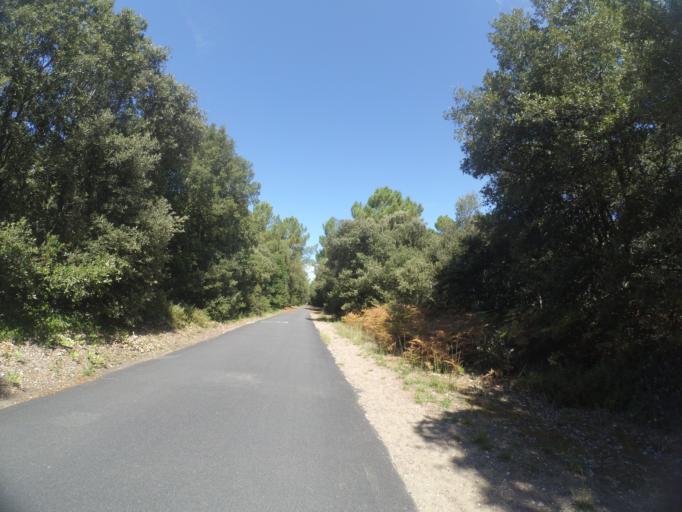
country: FR
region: Poitou-Charentes
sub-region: Departement de la Charente-Maritime
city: Les Mathes
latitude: 45.6741
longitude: -1.1502
